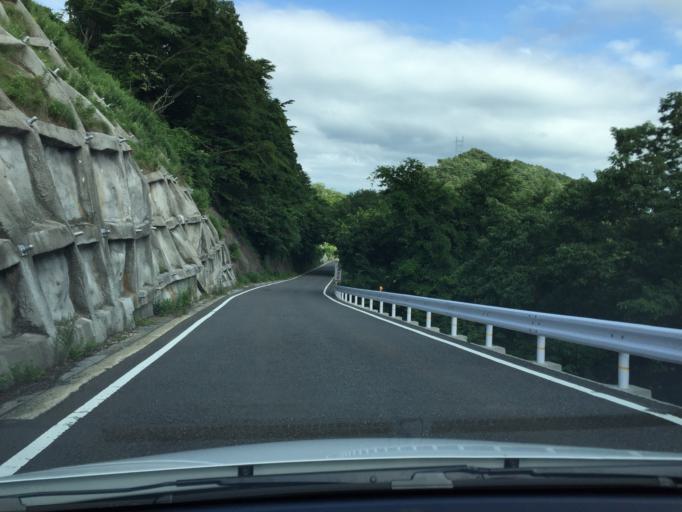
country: JP
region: Tochigi
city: Kuroiso
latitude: 37.2159
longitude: 140.0965
